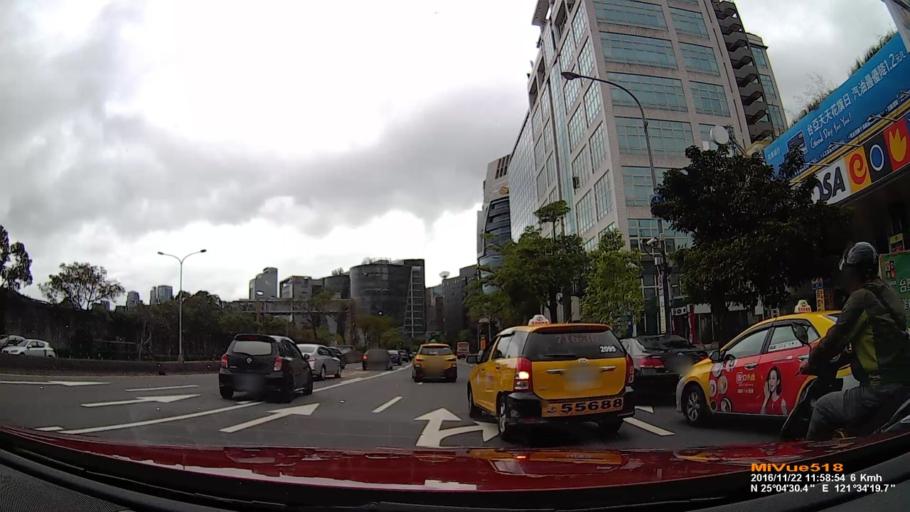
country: TW
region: Taipei
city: Taipei
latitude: 25.0751
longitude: 121.5721
